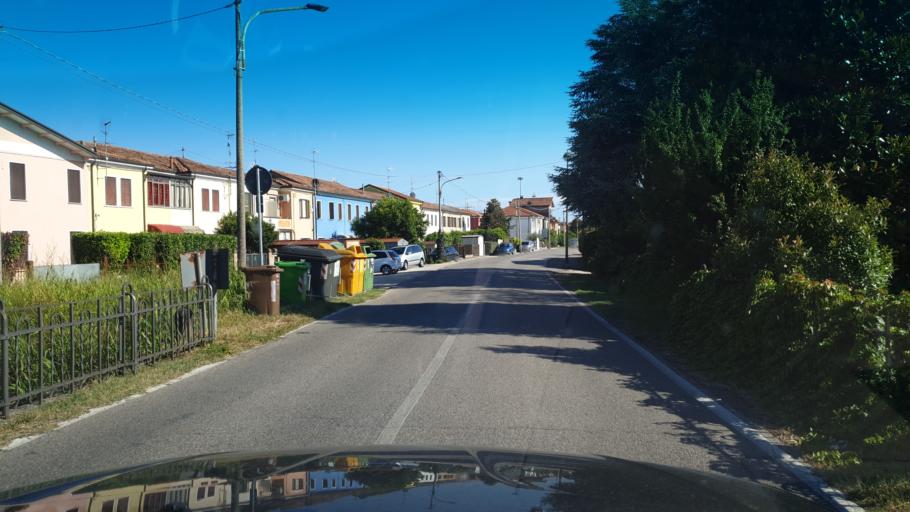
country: IT
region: Veneto
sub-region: Provincia di Rovigo
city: Rovigo
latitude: 45.0798
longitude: 11.7798
